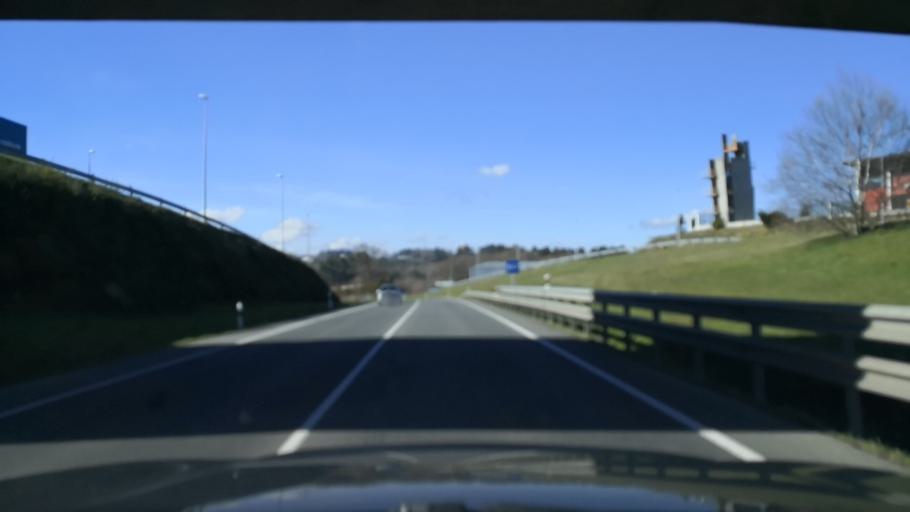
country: ES
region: Galicia
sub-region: Provincia de Pontevedra
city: Silleda
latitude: 42.6927
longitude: -8.2254
